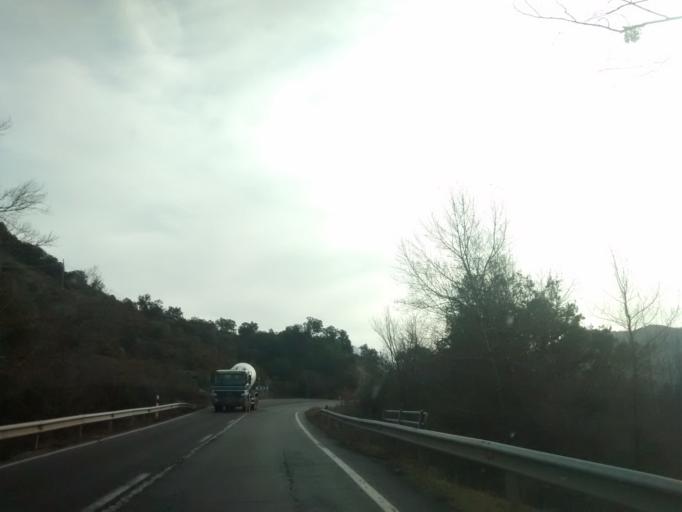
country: ES
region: Aragon
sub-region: Provincia de Huesca
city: Bailo
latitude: 42.5723
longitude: -0.8189
